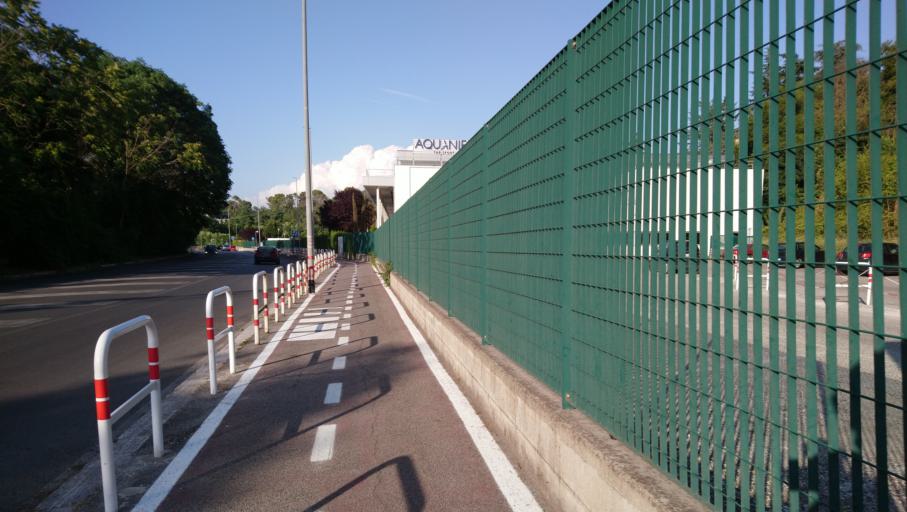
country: IT
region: Latium
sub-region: Citta metropolitana di Roma Capitale
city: Rome
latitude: 41.9321
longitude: 12.4905
